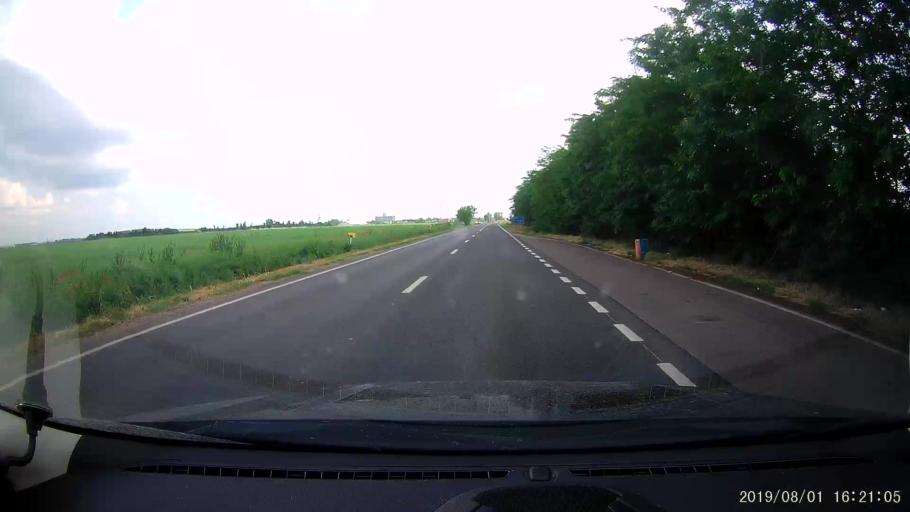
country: RO
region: Calarasi
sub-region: Municipiul Calarasi
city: Calarasi
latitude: 44.2209
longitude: 27.3406
